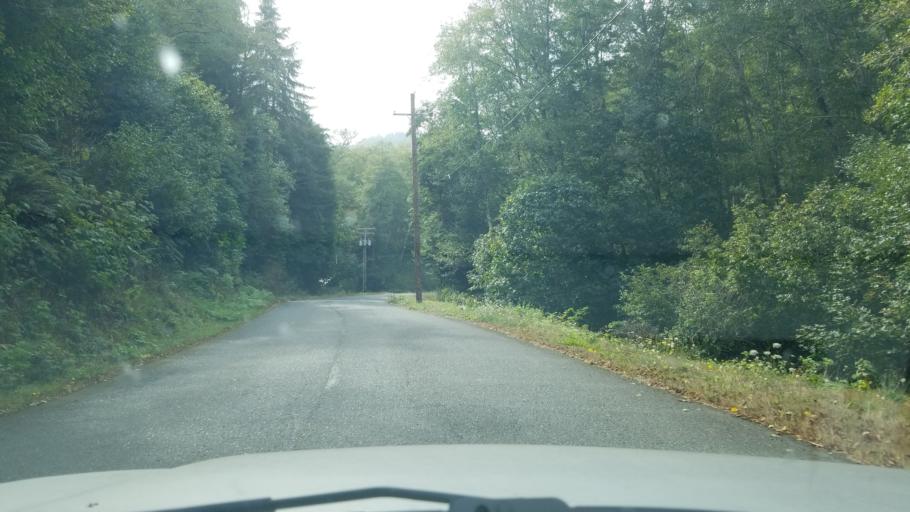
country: US
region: California
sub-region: Del Norte County
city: Bertsch-Oceanview
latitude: 41.5123
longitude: -124.0342
